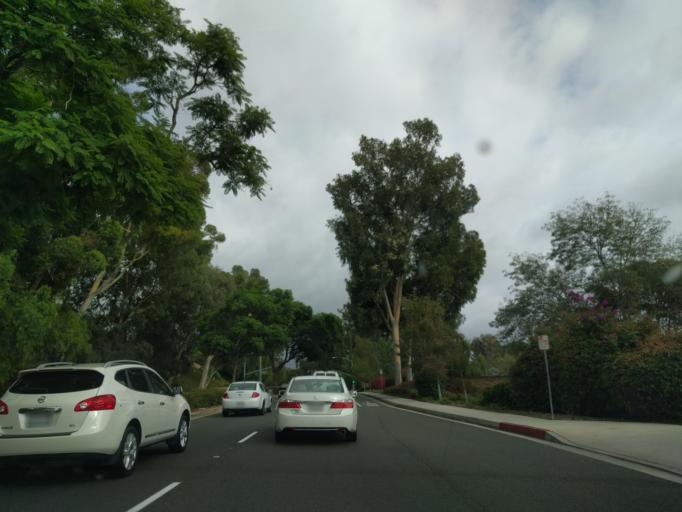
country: US
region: California
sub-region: Orange County
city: Mission Viejo
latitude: 33.5992
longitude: -117.6675
